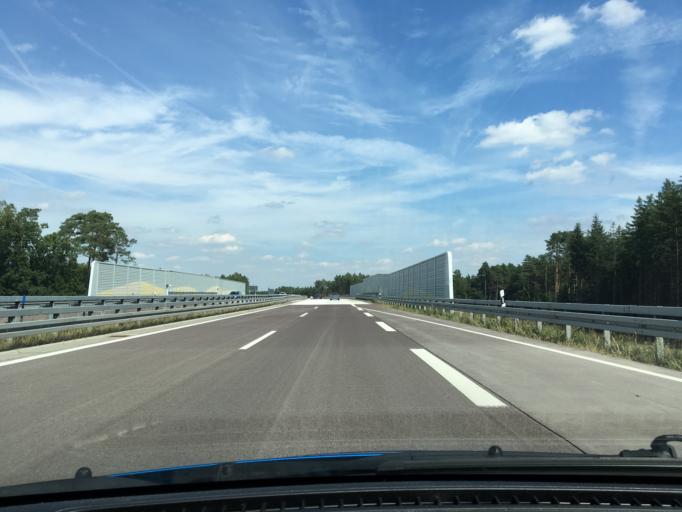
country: DE
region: Mecklenburg-Vorpommern
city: Gross Laasch
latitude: 53.3867
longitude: 11.5286
